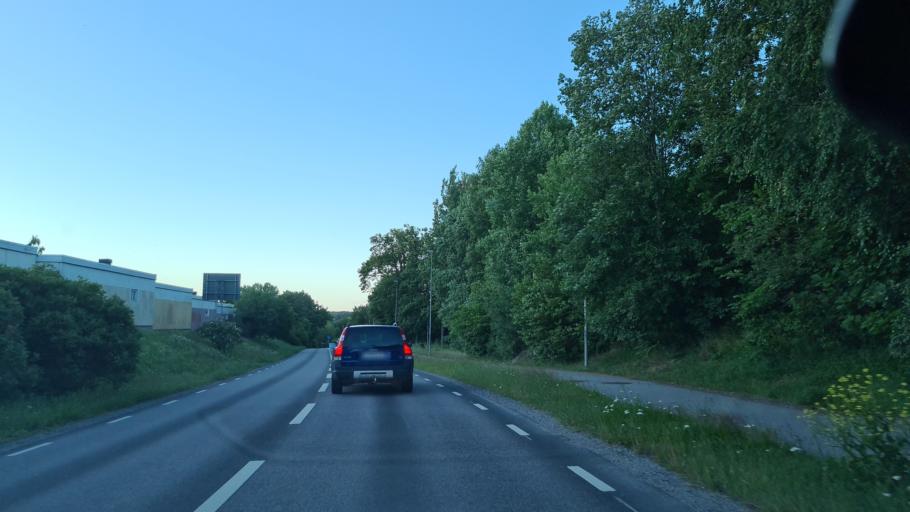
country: SE
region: Stockholm
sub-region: Nacka Kommun
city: Alta
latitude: 59.2527
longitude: 18.1769
